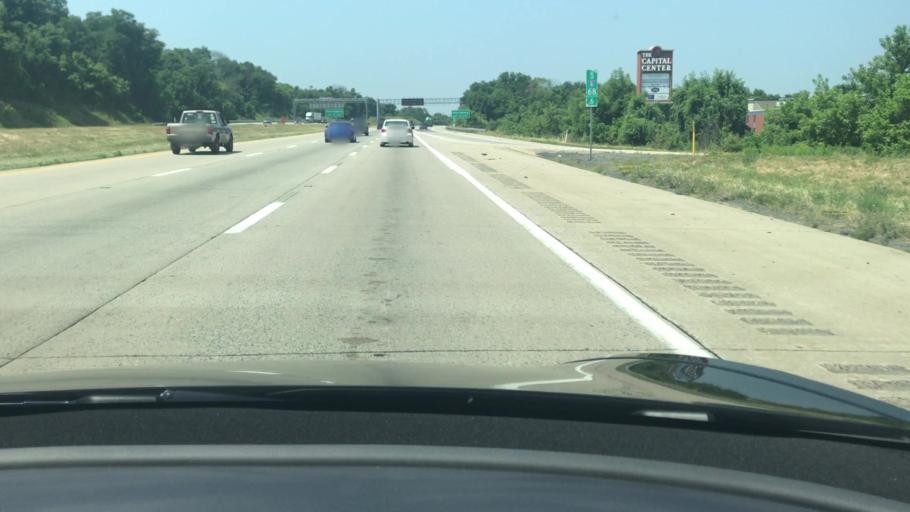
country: US
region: Pennsylvania
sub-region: Dauphin County
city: Penbrook
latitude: 40.3029
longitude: -76.8530
